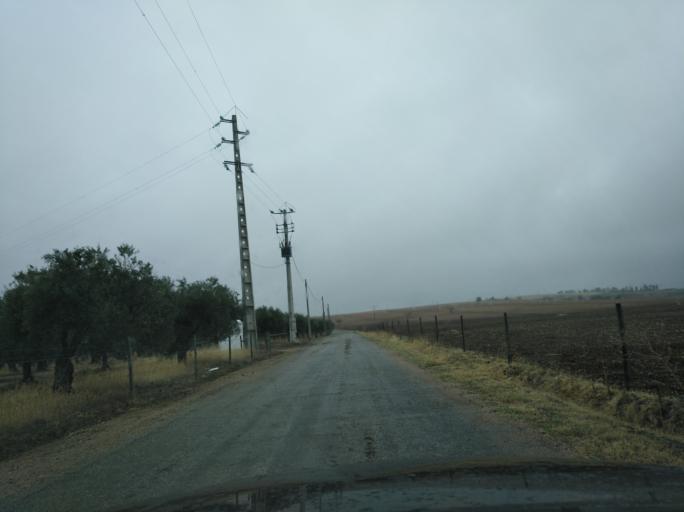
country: PT
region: Portalegre
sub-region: Campo Maior
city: Campo Maior
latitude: 38.9770
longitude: -7.0880
